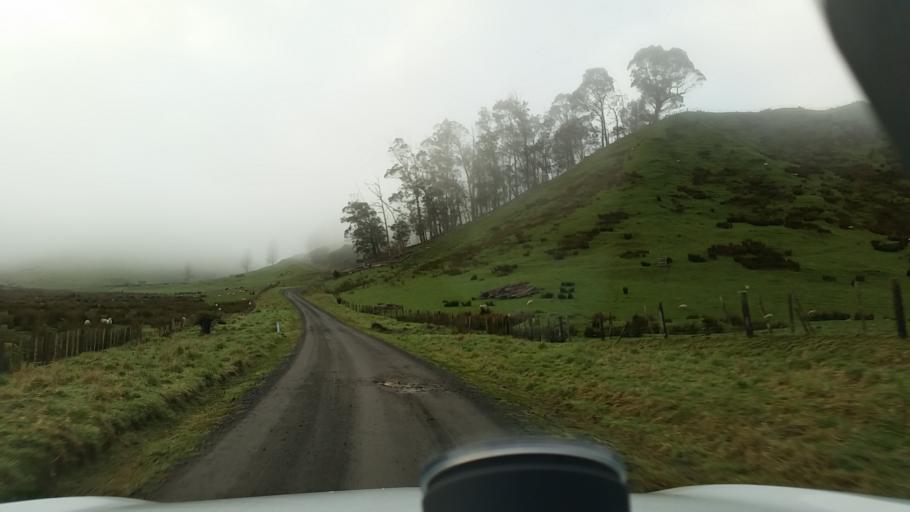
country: NZ
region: Taranaki
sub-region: South Taranaki District
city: Eltham
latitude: -39.4316
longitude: 174.4424
